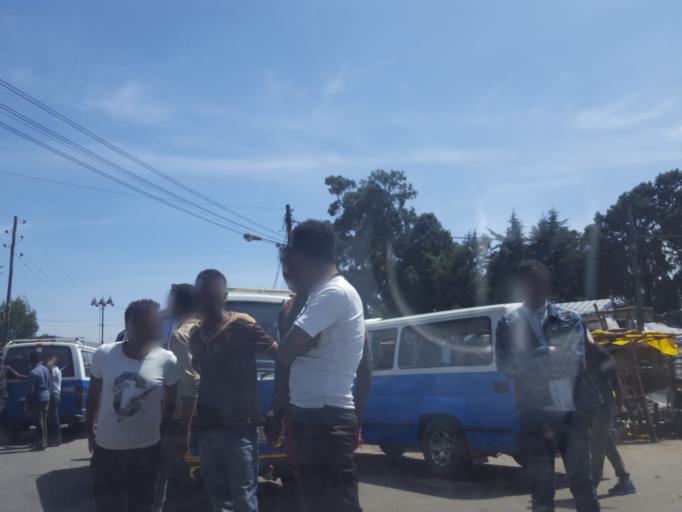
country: ET
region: Adis Abeba
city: Addis Ababa
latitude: 9.0589
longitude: 38.7274
